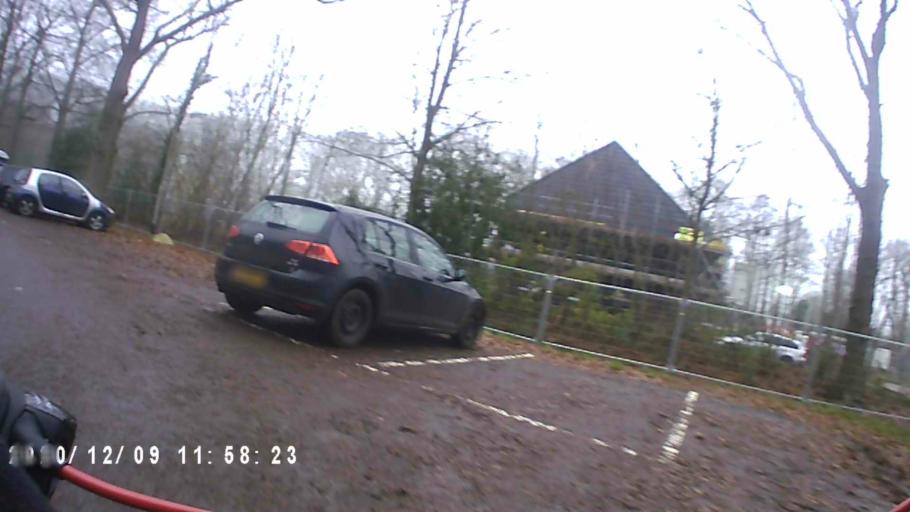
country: NL
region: Groningen
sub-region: Gemeente Haren
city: Haren
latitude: 53.1855
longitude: 6.5944
